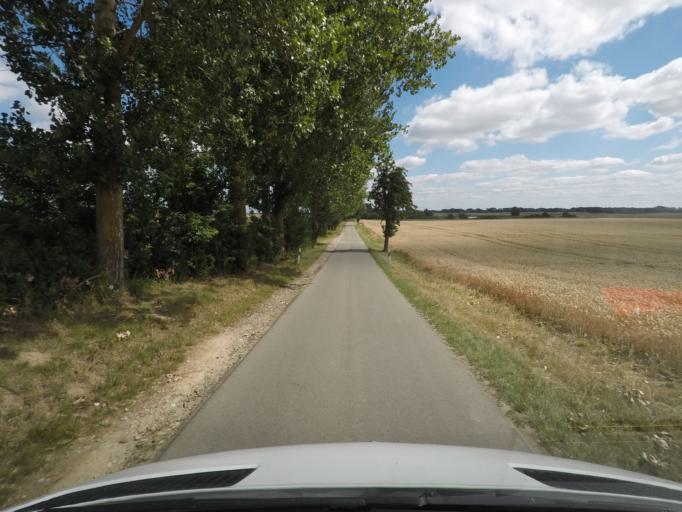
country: DE
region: Brandenburg
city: Brussow
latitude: 53.3689
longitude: 14.1307
